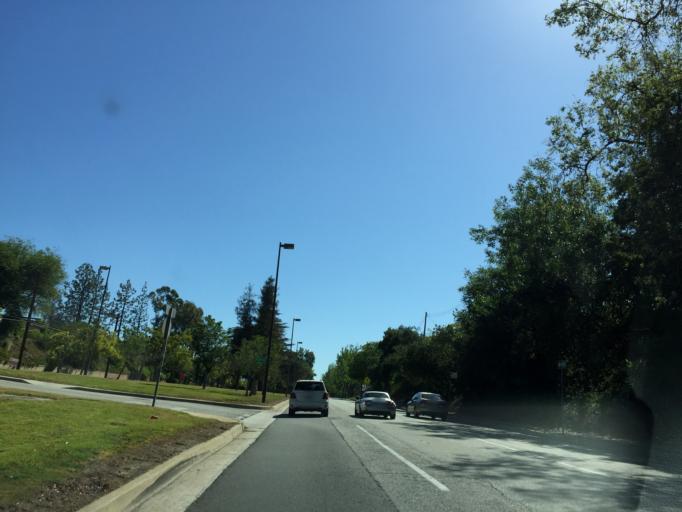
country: US
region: California
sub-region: Los Angeles County
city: East Pasadena
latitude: 34.1616
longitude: -118.0788
